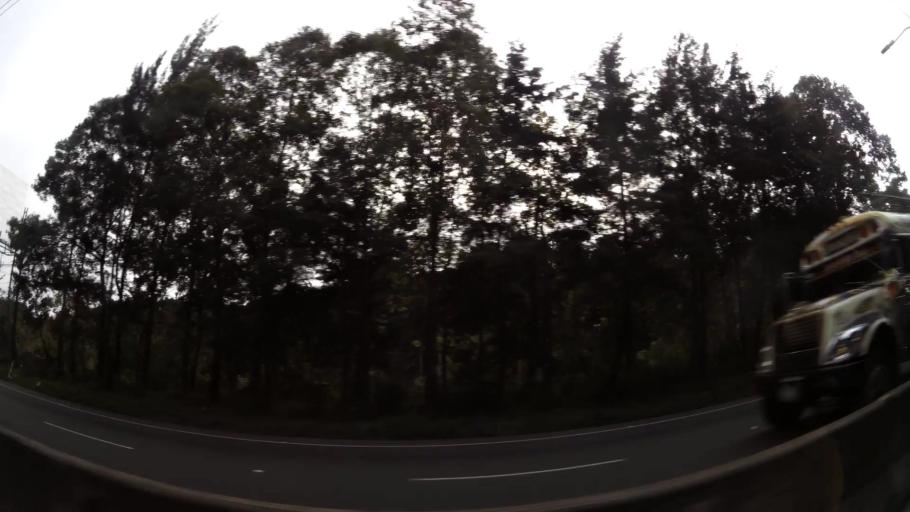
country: GT
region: Guatemala
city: Santa Catarina Pinula
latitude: 14.5776
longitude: -90.4717
